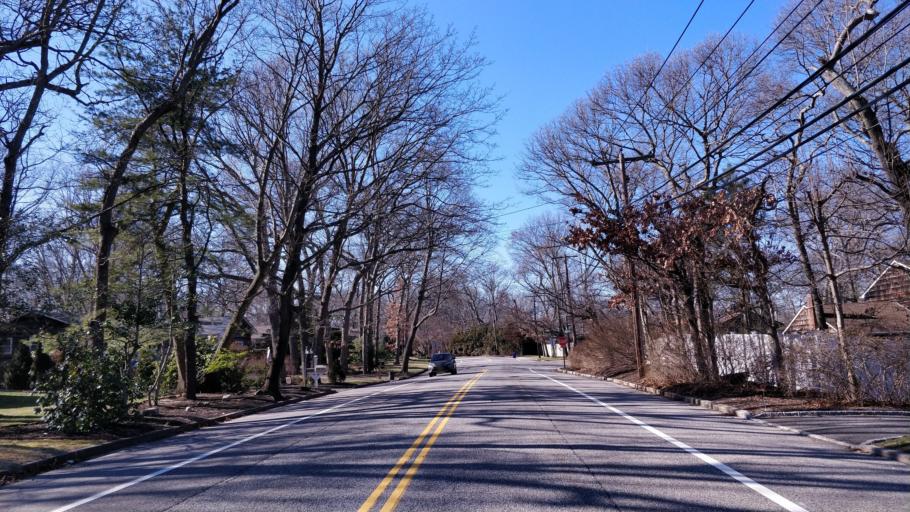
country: US
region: New York
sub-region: Suffolk County
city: Setauket-East Setauket
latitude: 40.9186
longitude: -73.0994
